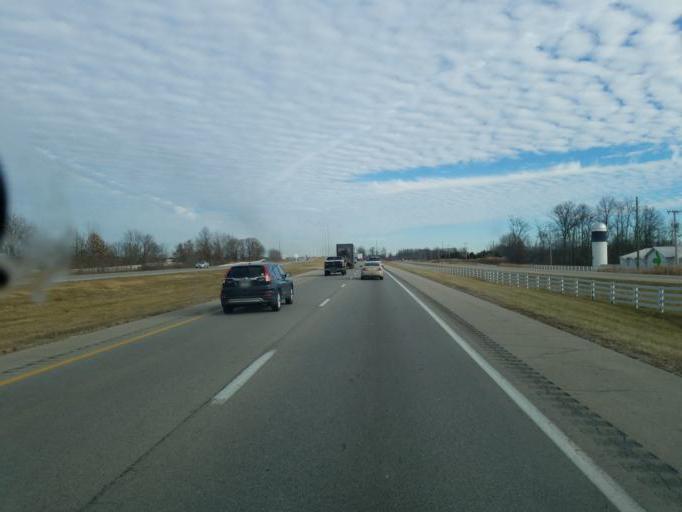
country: US
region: Ohio
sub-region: Franklin County
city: New Albany
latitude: 40.0794
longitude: -82.7682
